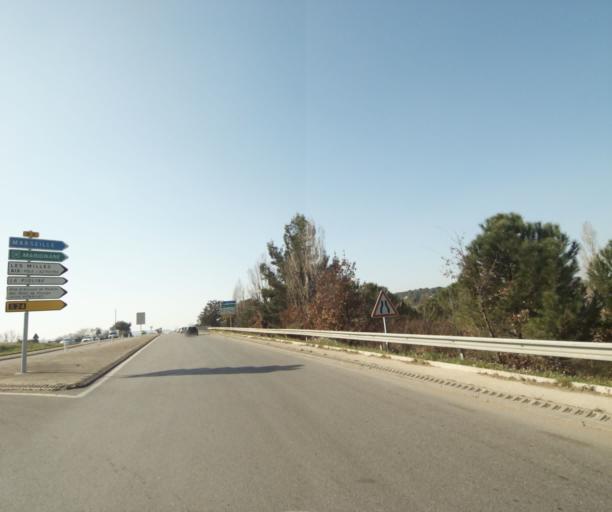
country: FR
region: Provence-Alpes-Cote d'Azur
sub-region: Departement des Bouches-du-Rhone
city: Aix-en-Provence
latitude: 43.5060
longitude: 5.4119
